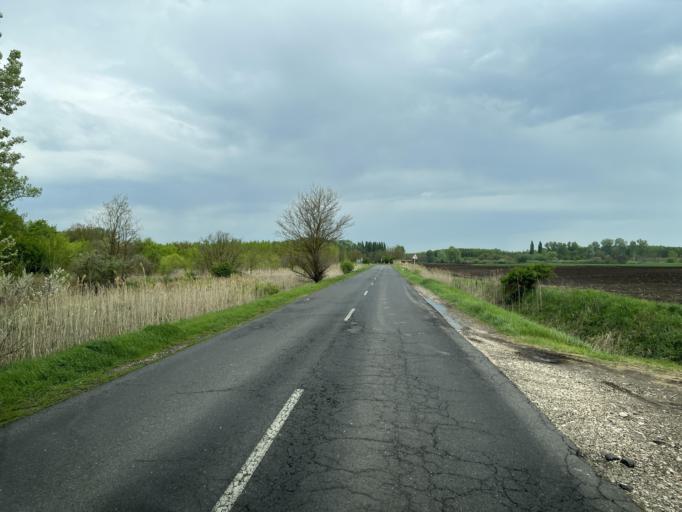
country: HU
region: Pest
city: Farmos
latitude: 47.3947
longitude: 19.8918
